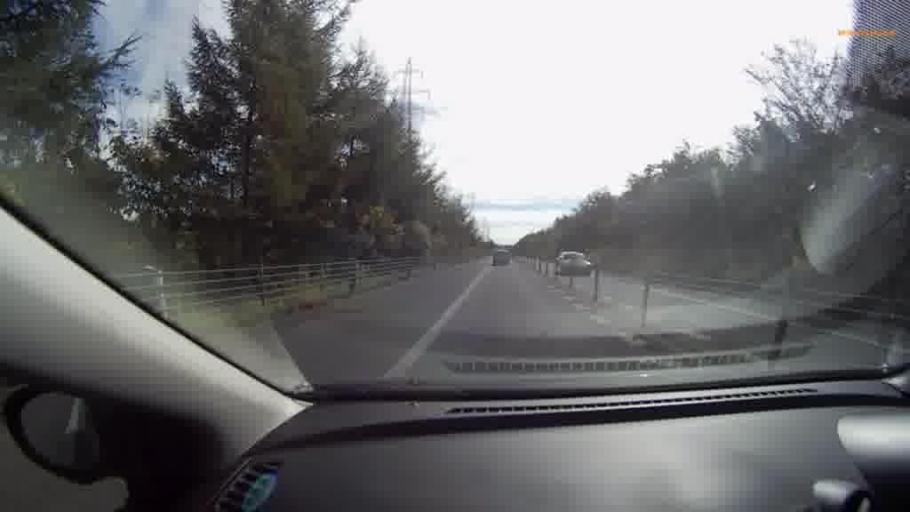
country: JP
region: Hokkaido
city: Kushiro
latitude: 43.0269
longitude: 144.4081
